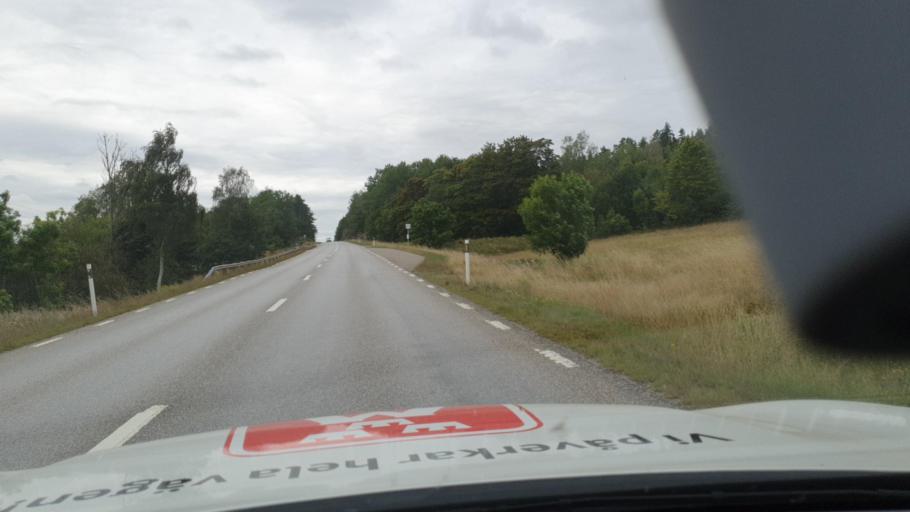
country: SE
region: Vaestra Goetaland
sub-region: Bengtsfors Kommun
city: Dals Langed
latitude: 58.7539
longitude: 12.2602
